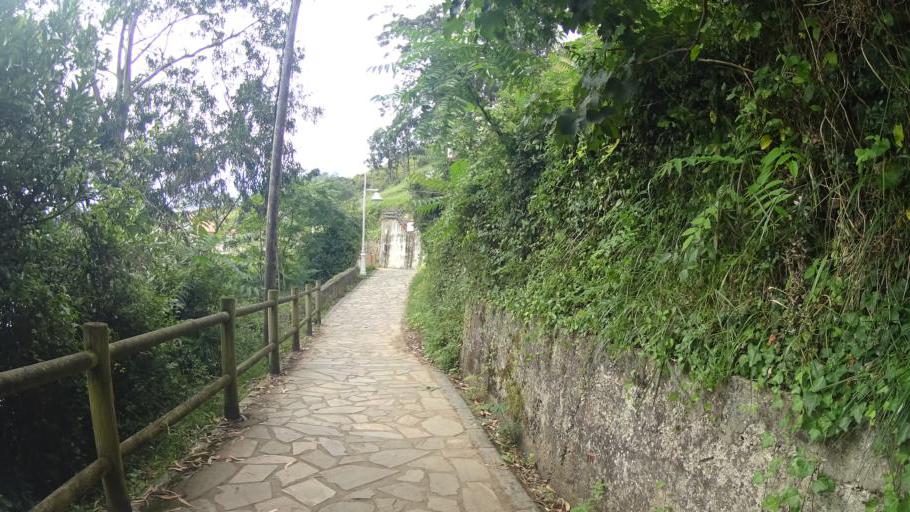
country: ES
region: Asturias
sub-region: Province of Asturias
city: Ribadesella
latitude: 43.4667
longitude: -5.0599
